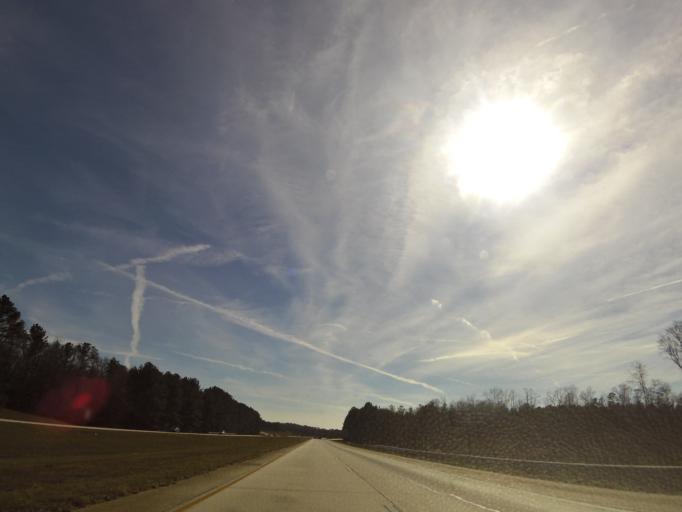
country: US
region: Georgia
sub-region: Troup County
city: Hogansville
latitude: 33.1687
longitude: -84.8663
